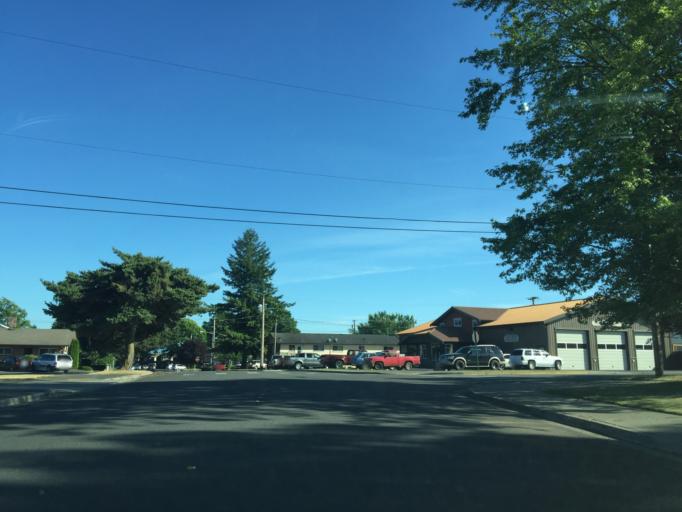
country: US
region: Washington
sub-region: Whatcom County
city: Lynden
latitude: 48.9461
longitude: -122.4507
